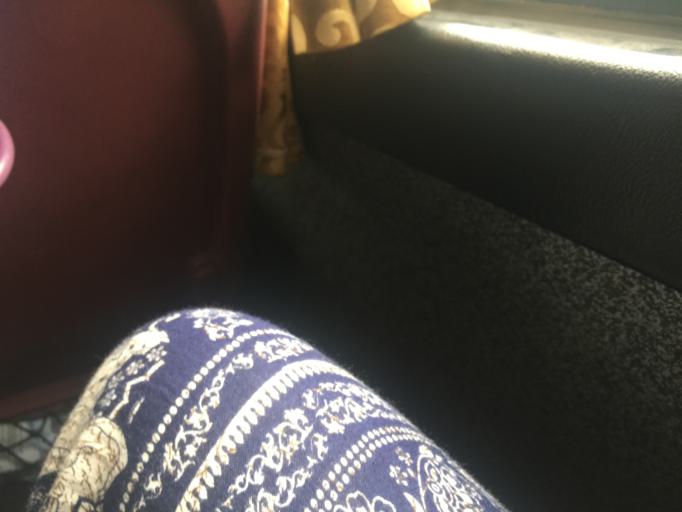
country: VN
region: Tay Ninh
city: Trang Bang
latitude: 11.1372
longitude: 106.4745
